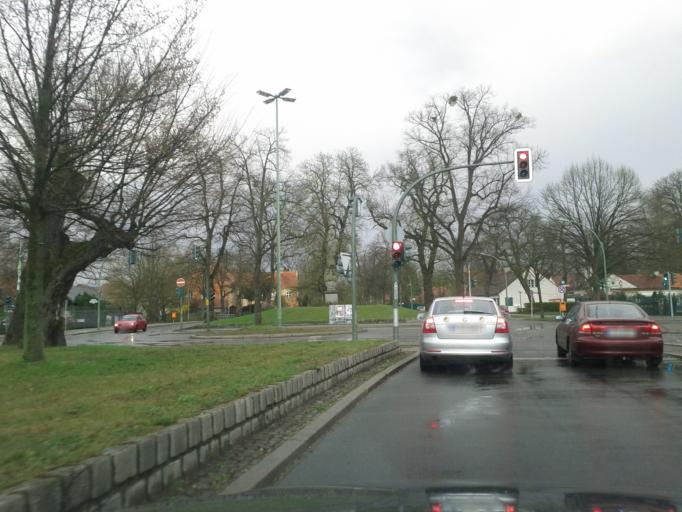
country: DE
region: Berlin
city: Dahlem
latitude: 52.4582
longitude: 13.2866
